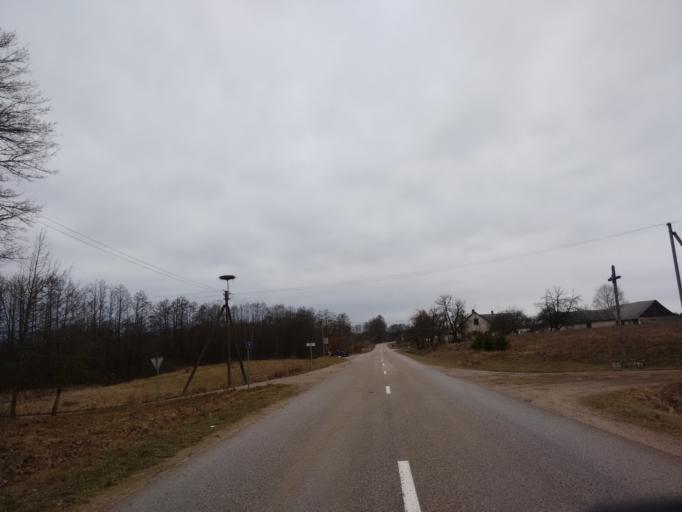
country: LT
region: Alytaus apskritis
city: Druskininkai
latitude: 54.2255
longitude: 23.8888
